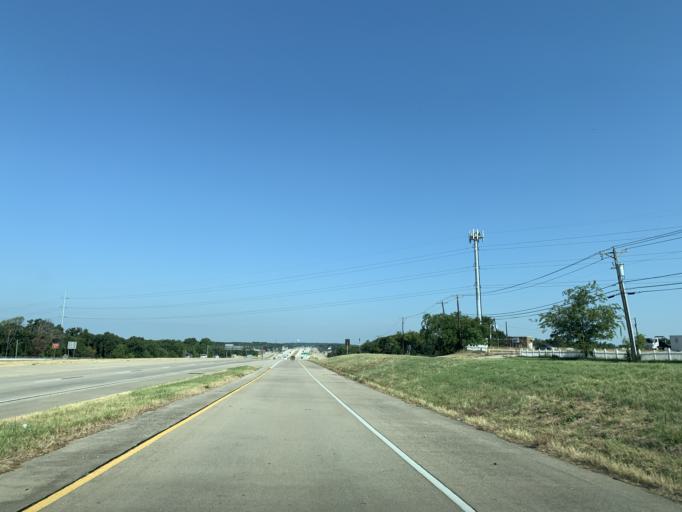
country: US
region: Texas
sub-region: Tarrant County
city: Lakeside
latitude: 32.8294
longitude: -97.4822
